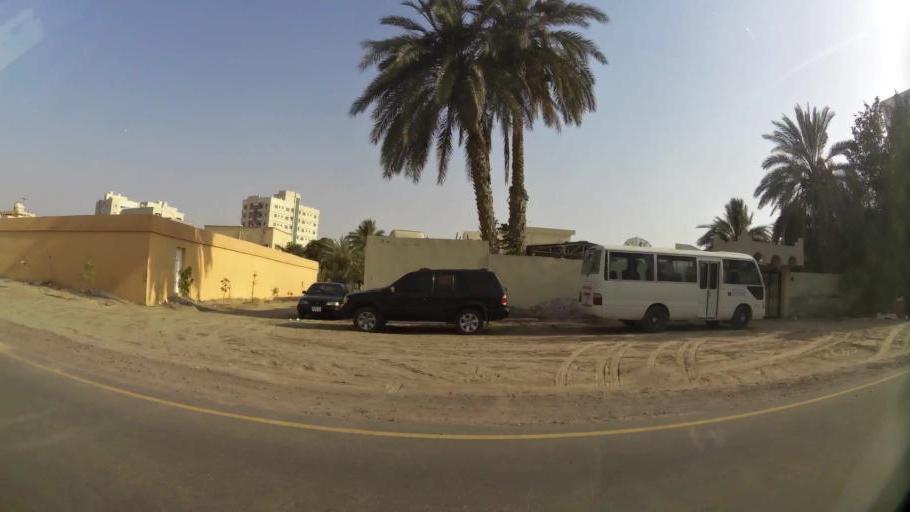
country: AE
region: Ajman
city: Ajman
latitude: 25.3878
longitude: 55.4408
